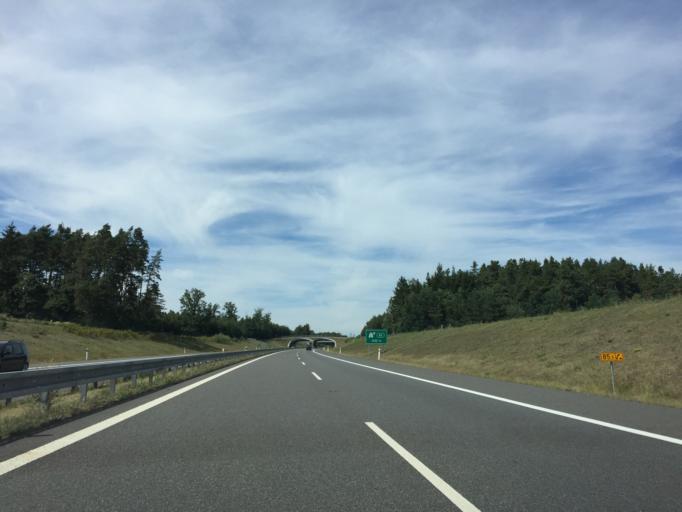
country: CZ
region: Jihocesky
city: Plana nad Luznici
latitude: 49.3523
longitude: 14.7264
